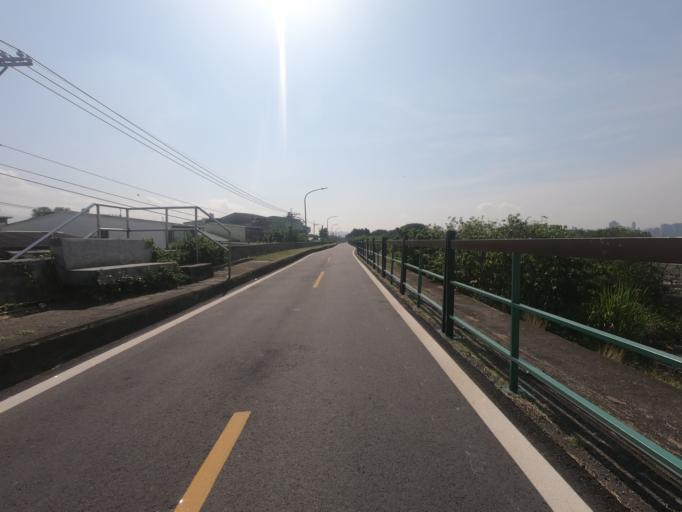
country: TW
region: Taipei
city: Taipei
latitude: 25.1060
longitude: 121.4734
